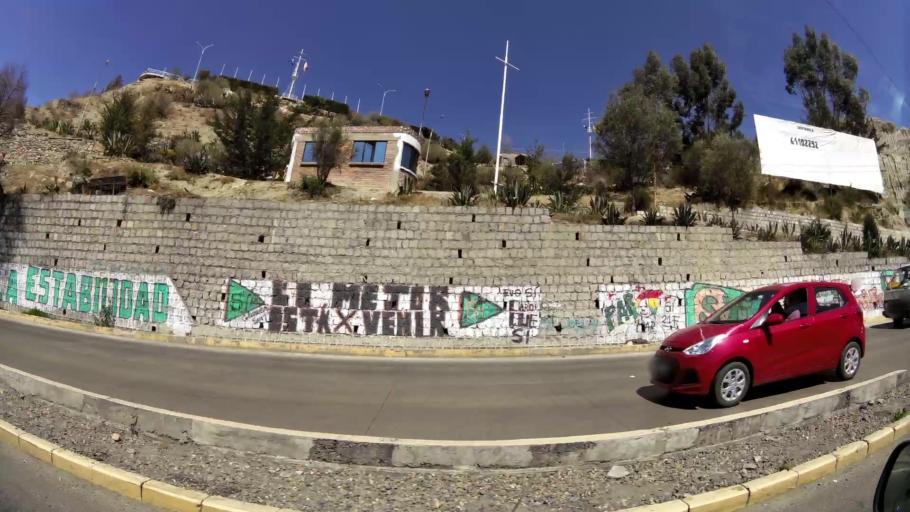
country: BO
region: La Paz
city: La Paz
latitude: -16.5153
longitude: -68.1229
